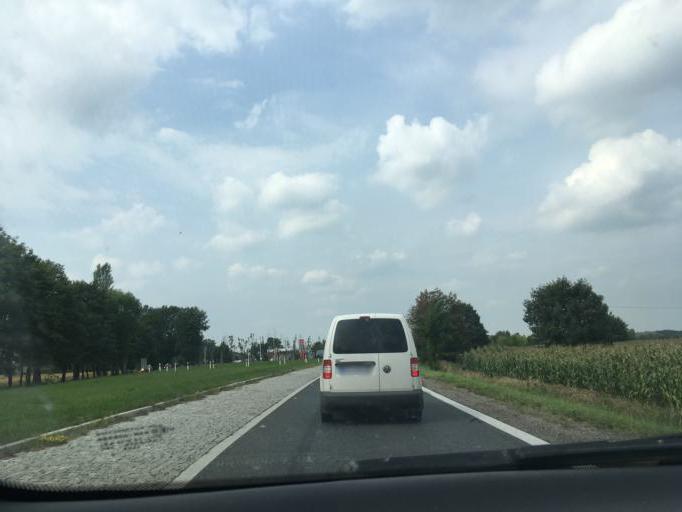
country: PL
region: Silesian Voivodeship
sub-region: Powiat bierunsko-ledzinski
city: Bierun
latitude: 50.0844
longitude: 19.1154
